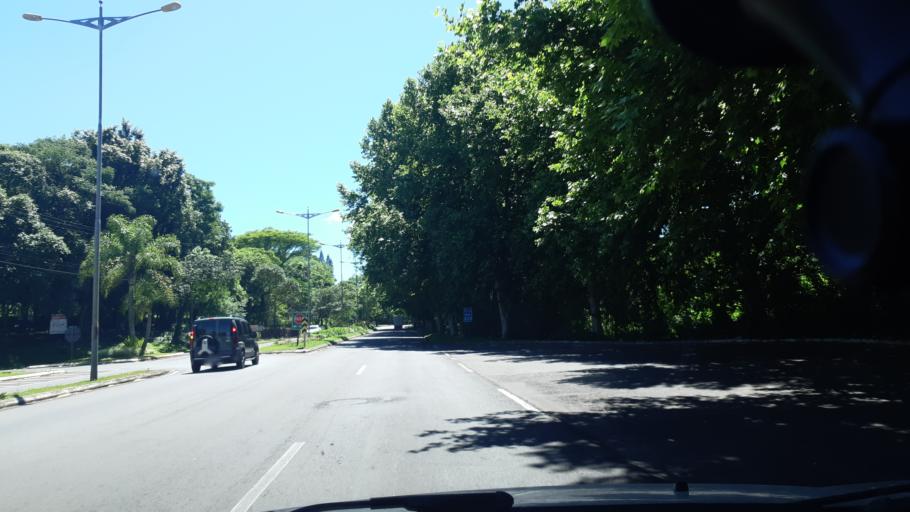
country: BR
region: Rio Grande do Sul
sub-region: Ivoti
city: Ivoti
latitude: -29.6253
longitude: -51.1362
